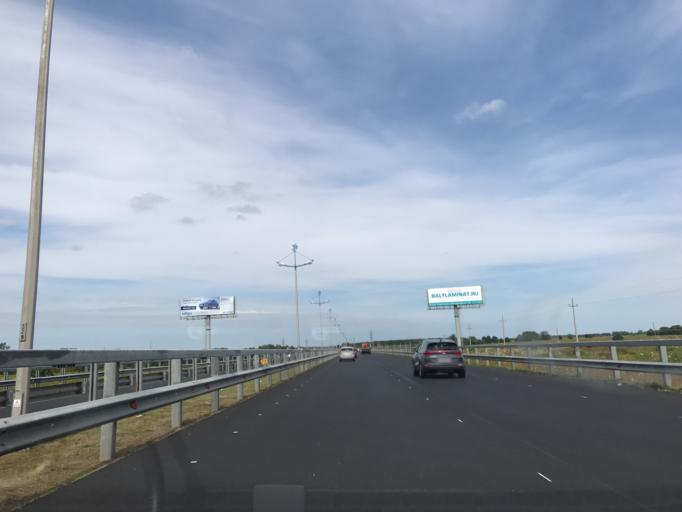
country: RU
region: Kaliningrad
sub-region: Zelenogradskiy Rayon
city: Zelenogradsk
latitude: 54.8857
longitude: 20.5296
